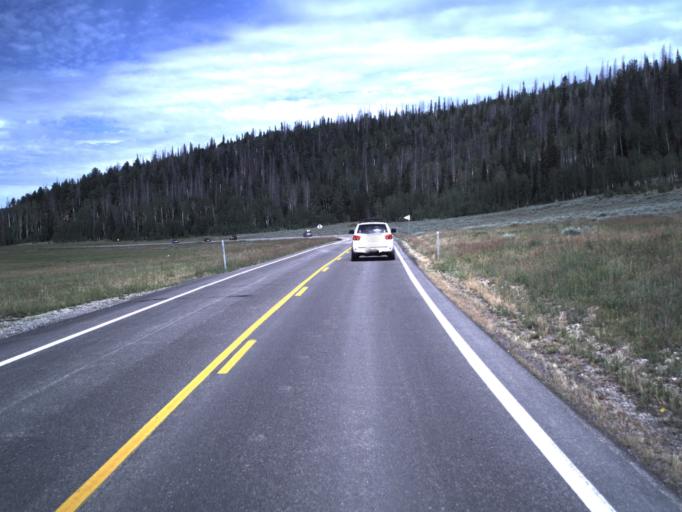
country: US
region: Utah
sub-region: Iron County
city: Parowan
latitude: 37.5704
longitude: -112.8058
